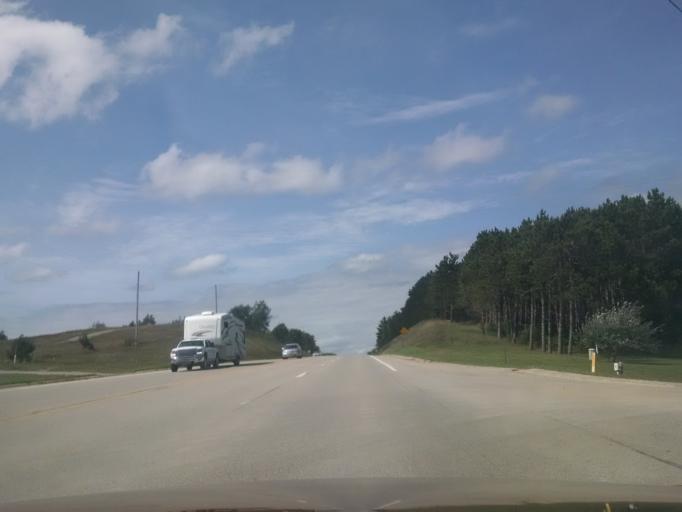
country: US
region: Michigan
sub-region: Clare County
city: Clare
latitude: 43.8895
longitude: -84.9630
